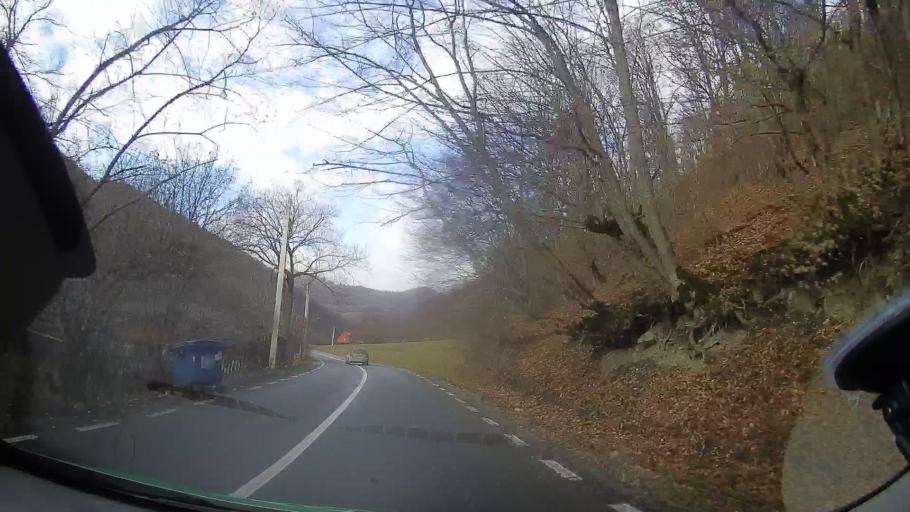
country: RO
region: Cluj
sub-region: Comuna Baisoara
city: Baisoara
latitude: 46.6102
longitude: 23.4152
